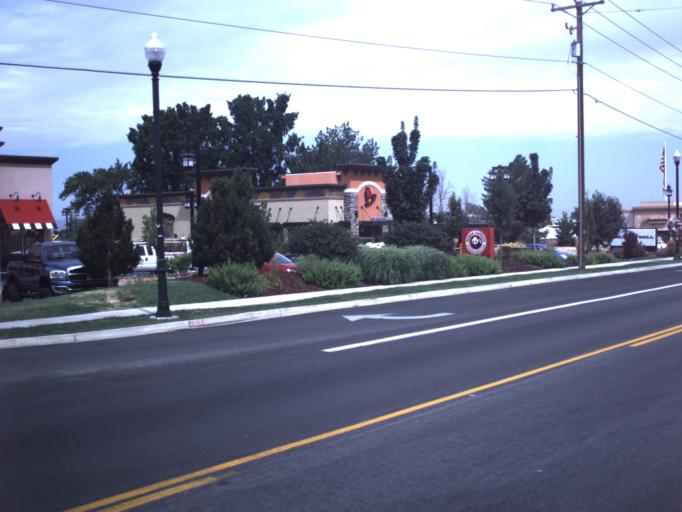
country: US
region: Utah
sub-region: Davis County
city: Clinton
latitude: 41.1374
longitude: -112.0644
